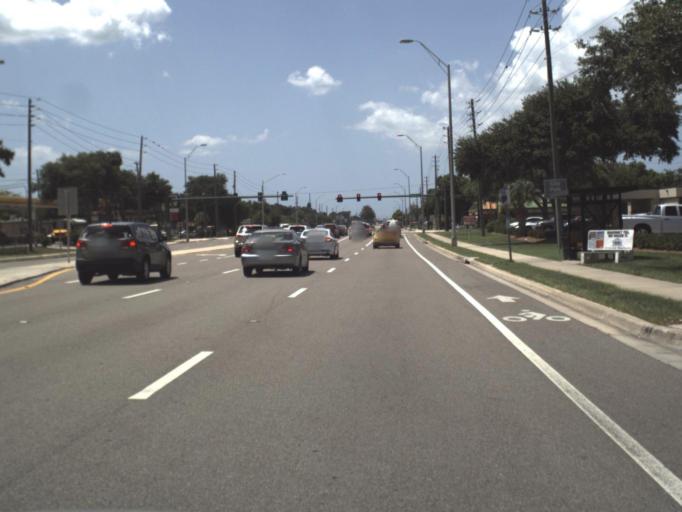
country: US
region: Florida
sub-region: Pinellas County
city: Ridgecrest
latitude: 27.8804
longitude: -82.8184
